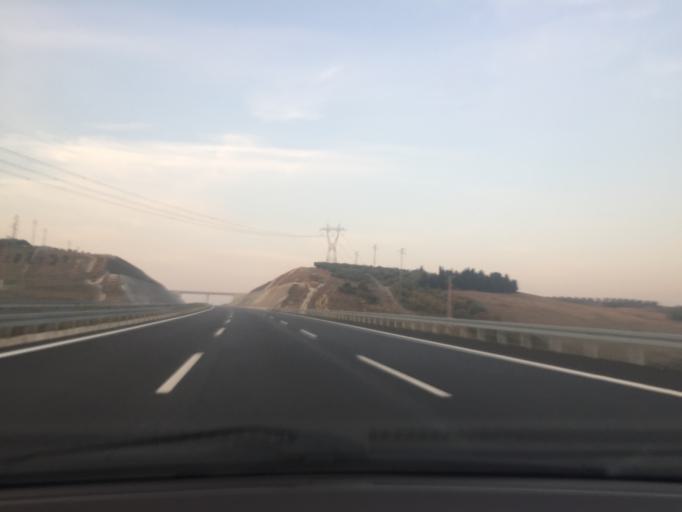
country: TR
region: Bursa
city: Mahmudiye
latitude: 40.2748
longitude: 28.5097
